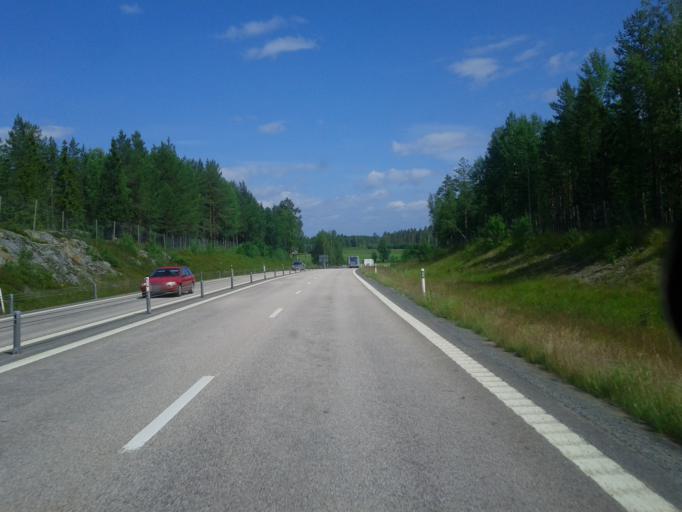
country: SE
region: Vaesterbotten
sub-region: Nordmalings Kommun
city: Nordmaling
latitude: 63.4957
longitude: 19.3219
